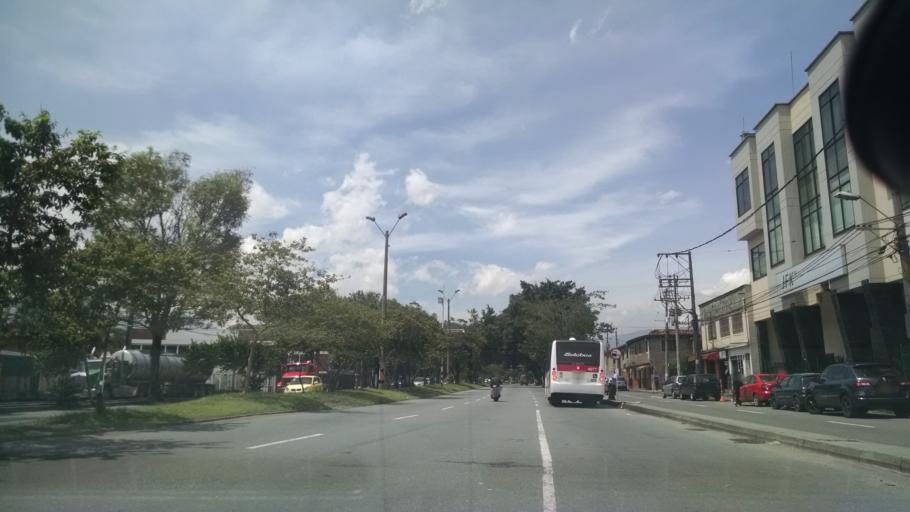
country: CO
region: Antioquia
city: Itagui
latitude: 6.2132
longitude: -75.5829
